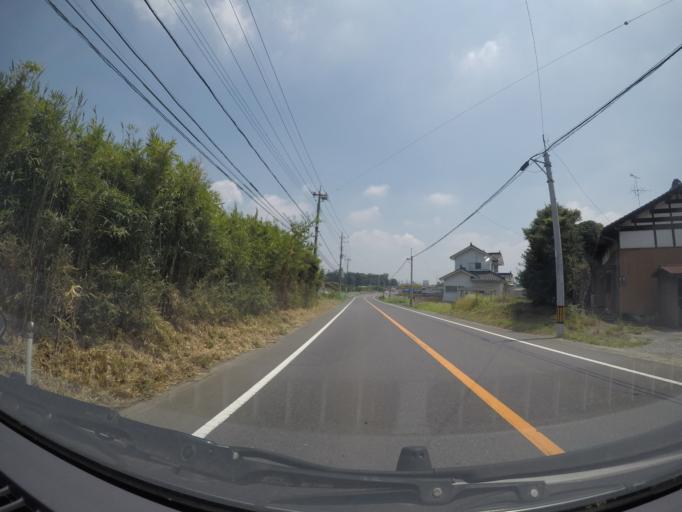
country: JP
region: Ibaraki
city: Koga
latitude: 36.2014
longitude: 139.8016
